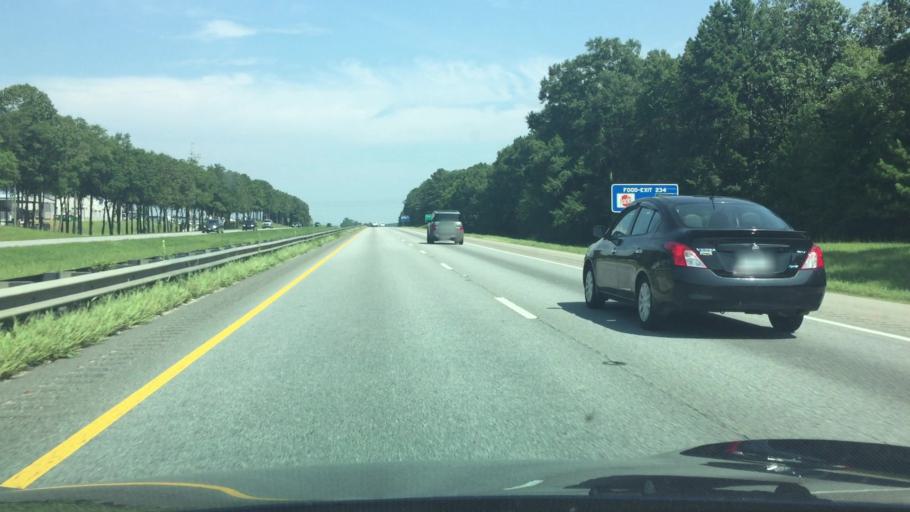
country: US
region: Alabama
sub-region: Shelby County
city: Calera
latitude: 33.1622
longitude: -86.7721
